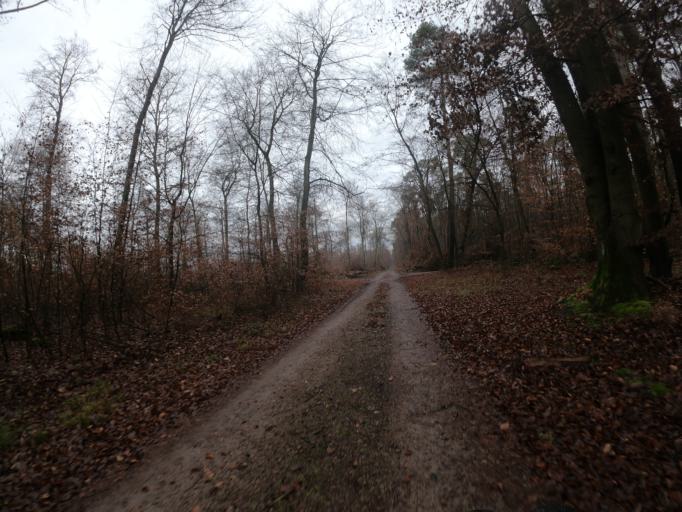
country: DE
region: Hesse
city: Morfelden-Walldorf
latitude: 49.9801
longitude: 8.6076
